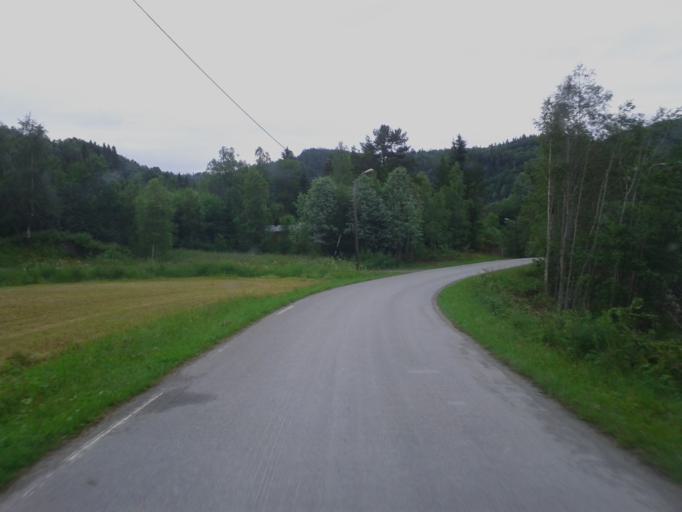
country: NO
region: Sor-Trondelag
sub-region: Melhus
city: Lundamo
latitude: 63.1373
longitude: 10.3267
